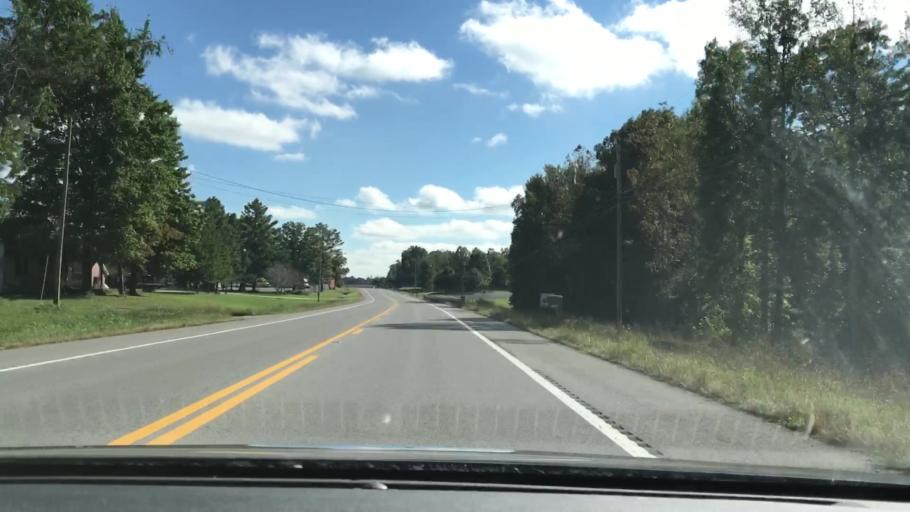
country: US
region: Tennessee
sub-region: Fentress County
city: Grimsley
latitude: 36.2778
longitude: -84.9819
